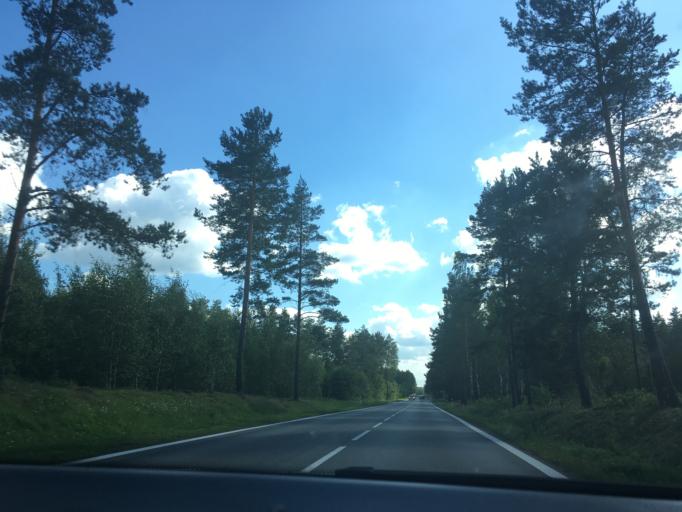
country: PL
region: Podlasie
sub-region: Powiat sokolski
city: Janow
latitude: 53.3607
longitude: 23.1042
